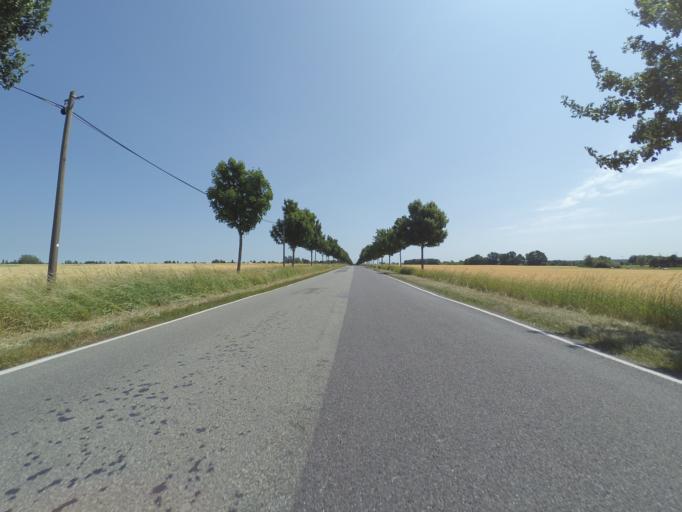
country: DE
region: Brandenburg
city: Gerdshagen
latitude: 53.3089
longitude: 12.2828
